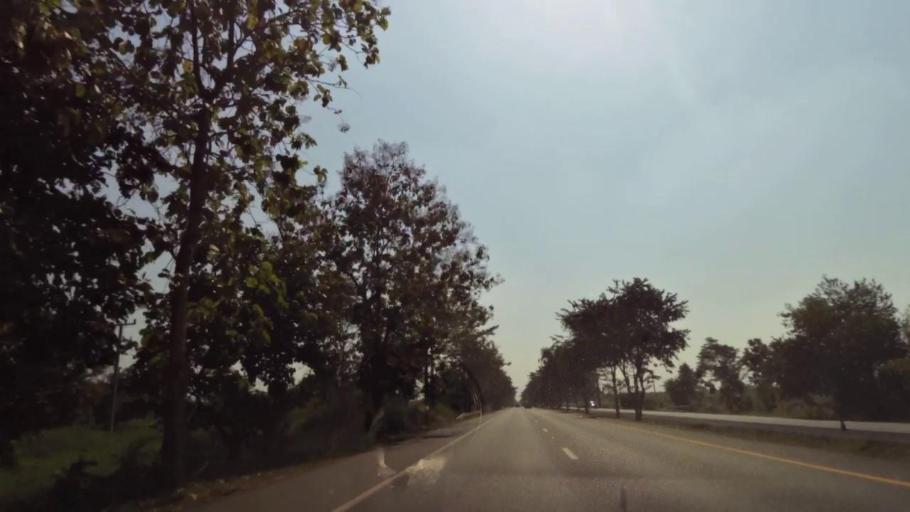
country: TH
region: Phichit
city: Bueng Na Rang
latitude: 16.0849
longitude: 100.1248
